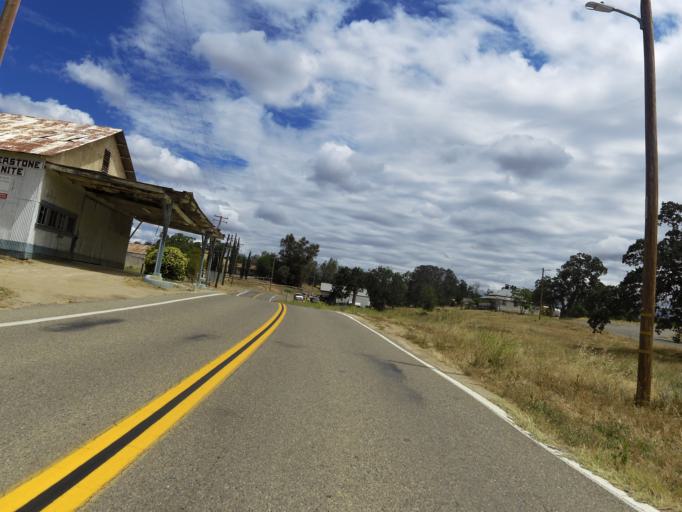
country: US
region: California
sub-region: Madera County
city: Yosemite Lakes
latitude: 37.2180
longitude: -119.9063
